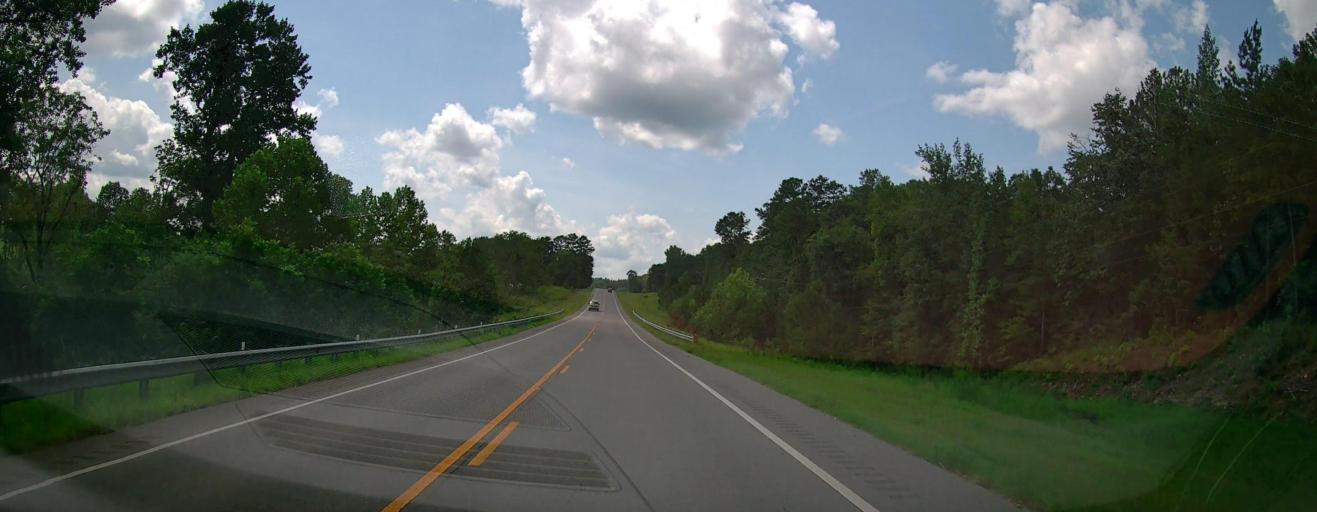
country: US
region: Alabama
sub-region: Cleburne County
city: Heflin
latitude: 33.5800
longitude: -85.4642
